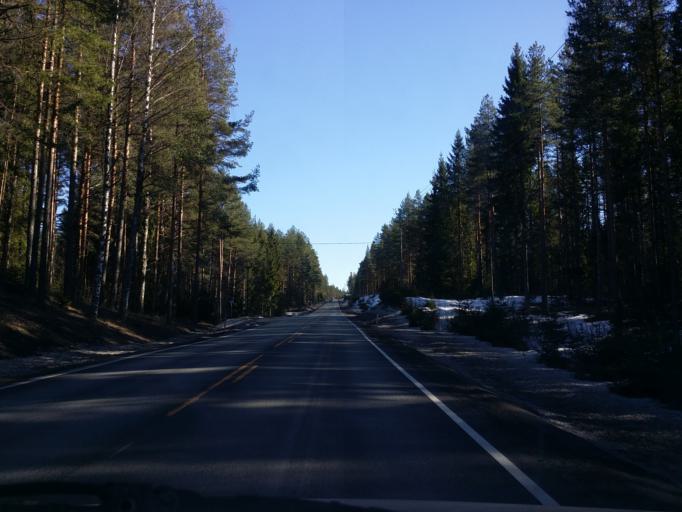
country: NO
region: Buskerud
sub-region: Ringerike
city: Honefoss
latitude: 60.3203
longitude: 10.1377
